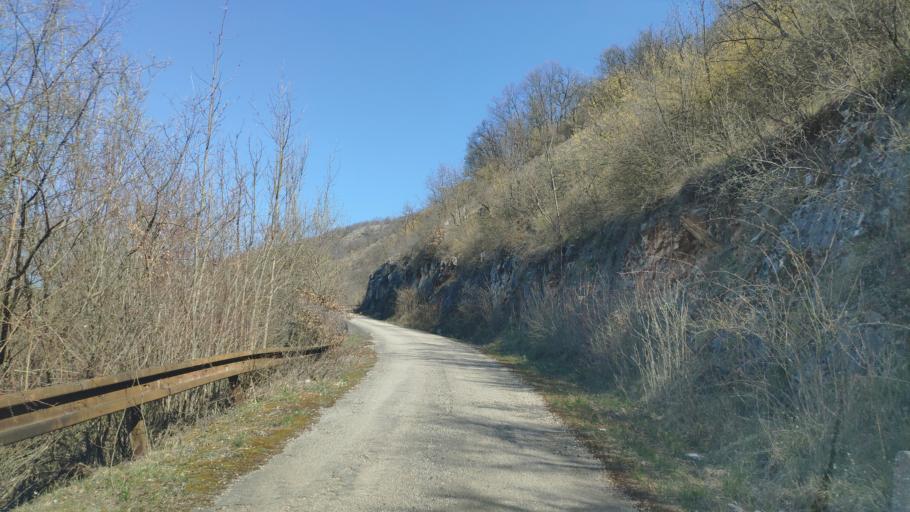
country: SK
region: Kosicky
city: Roznava
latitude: 48.5708
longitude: 20.4053
